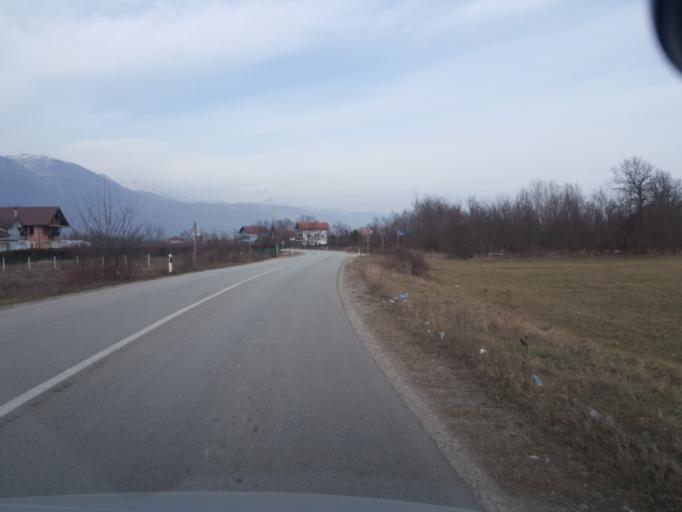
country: XK
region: Pec
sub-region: Komuna e Istogut
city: Istok
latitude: 42.7430
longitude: 20.4850
